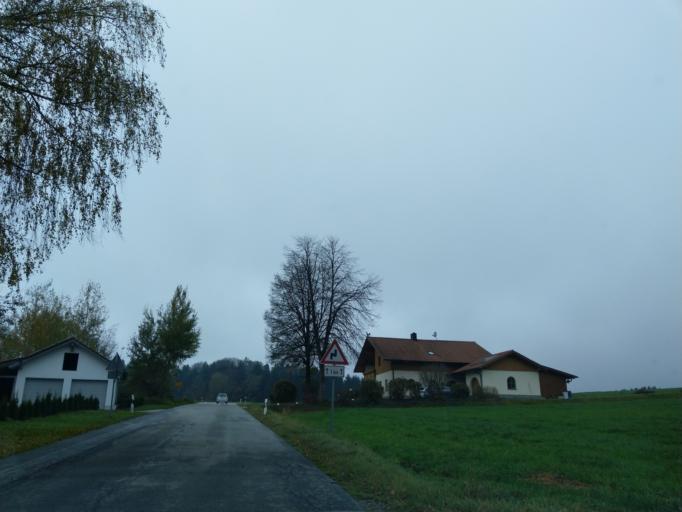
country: DE
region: Bavaria
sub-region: Lower Bavaria
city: Schollnach
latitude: 48.7736
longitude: 13.1713
